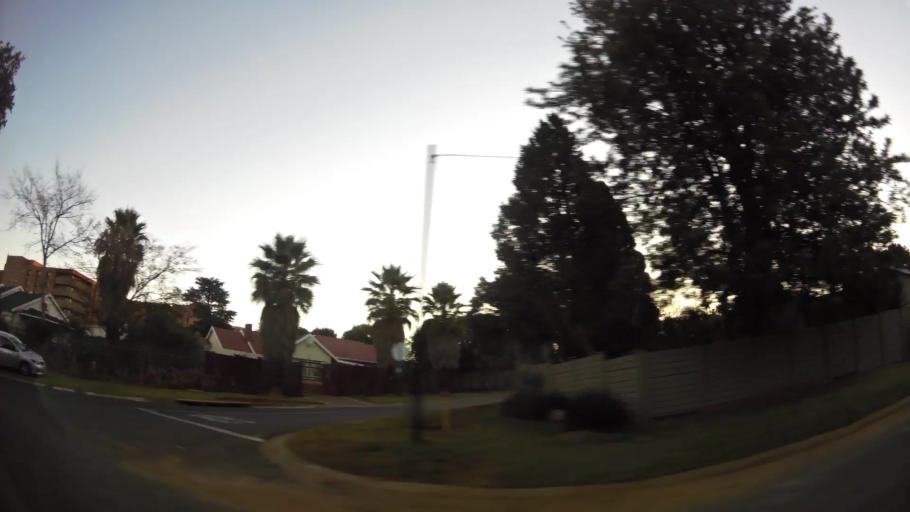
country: ZA
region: Gauteng
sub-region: City of Johannesburg Metropolitan Municipality
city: Roodepoort
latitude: -26.1566
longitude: 27.9049
